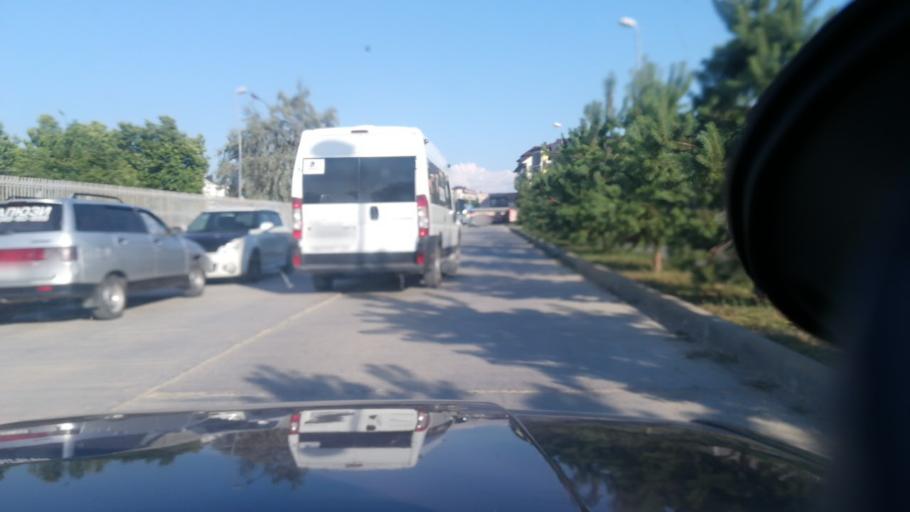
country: RU
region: Krasnodarskiy
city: Vityazevo
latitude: 44.9884
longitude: 37.2490
